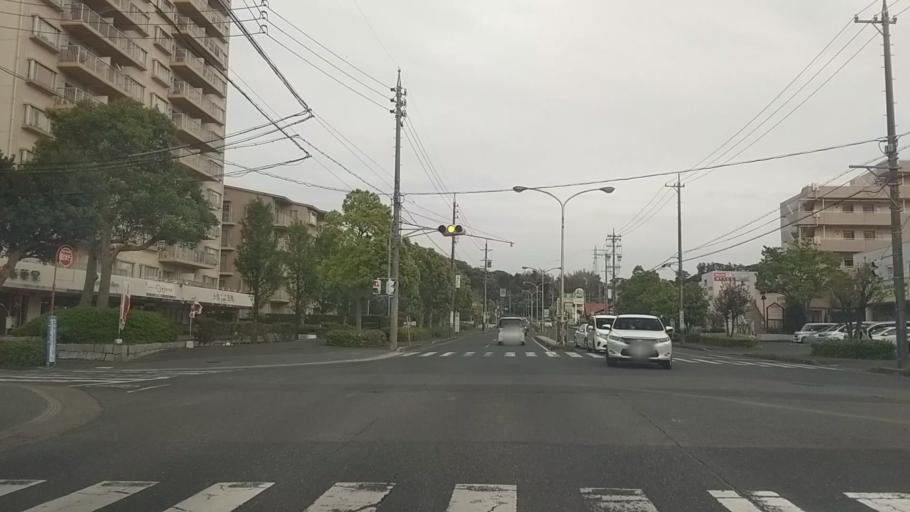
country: JP
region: Shizuoka
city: Hamamatsu
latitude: 34.7227
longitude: 137.6996
